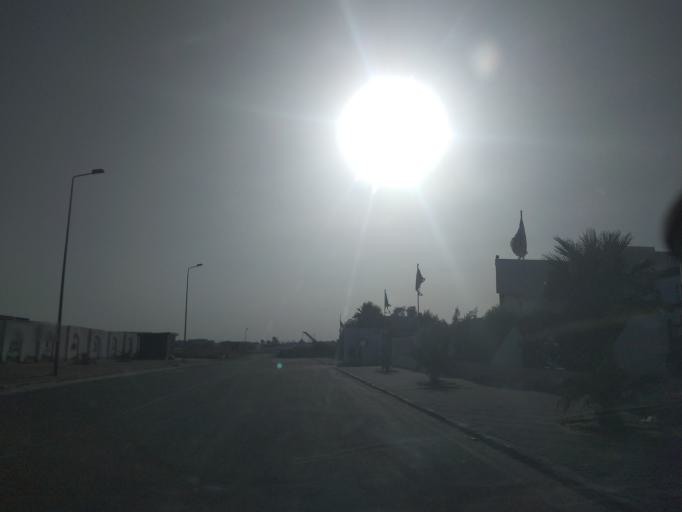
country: TN
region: Safaqis
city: Sfax
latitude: 34.7251
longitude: 10.7539
